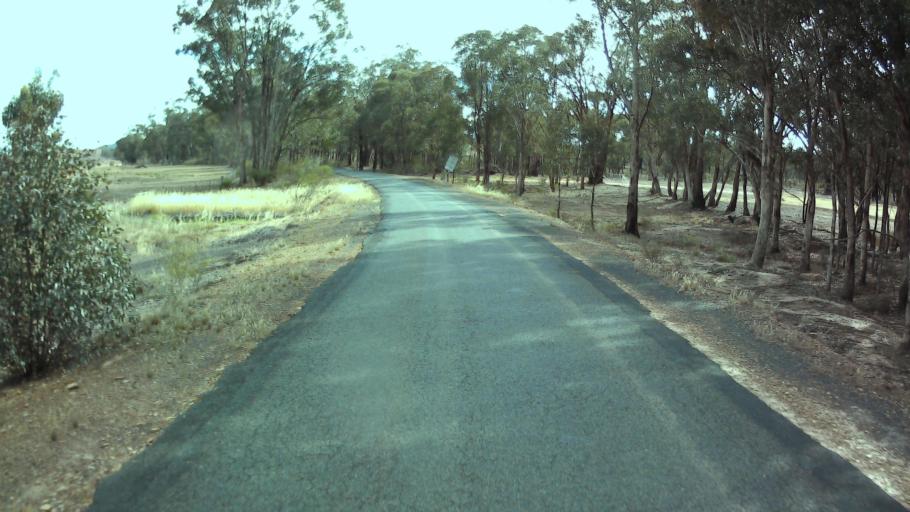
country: AU
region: New South Wales
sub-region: Weddin
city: Grenfell
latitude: -33.8484
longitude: 148.2334
